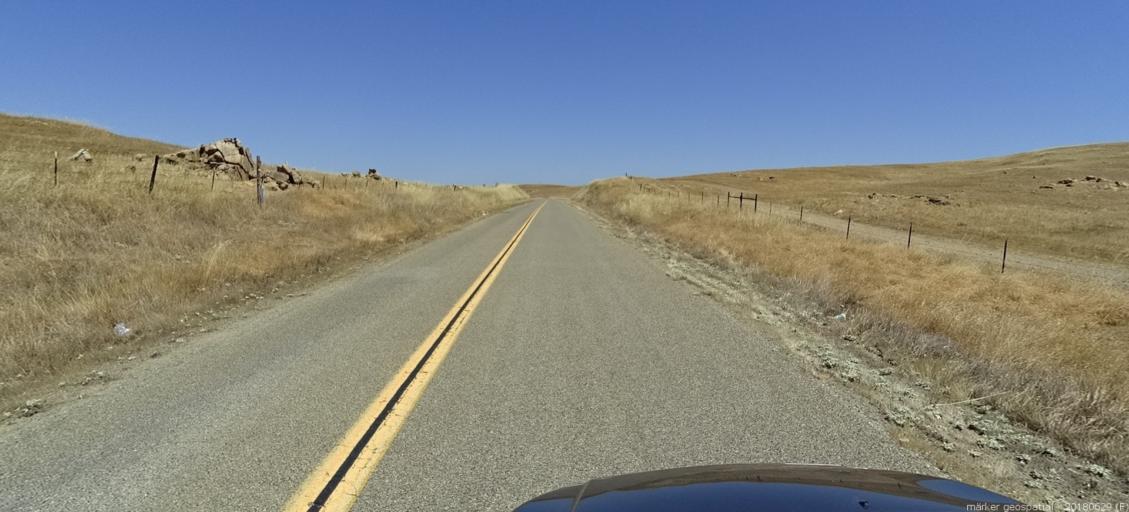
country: US
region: California
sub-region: Madera County
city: Bonadelle Ranchos-Madera Ranchos
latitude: 37.0861
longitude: -119.8812
